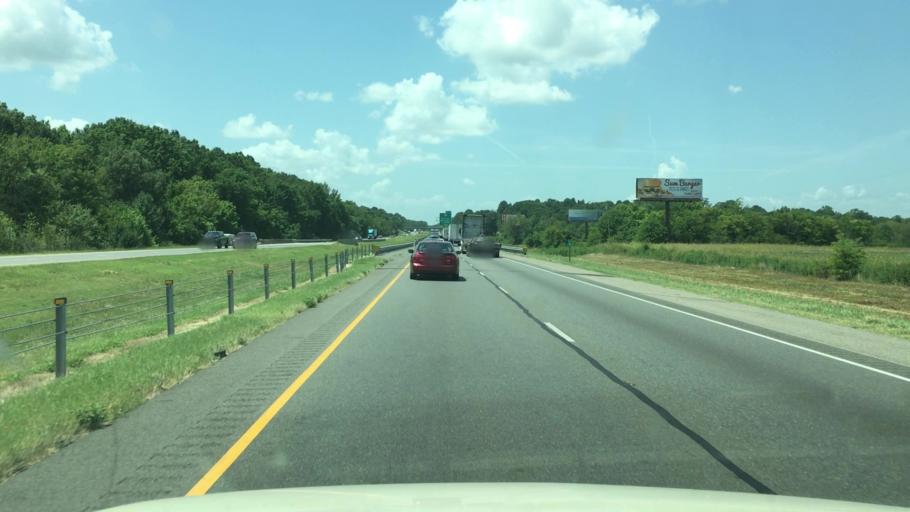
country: US
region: Arkansas
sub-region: Miller County
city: Texarkana
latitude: 33.4954
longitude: -93.9645
